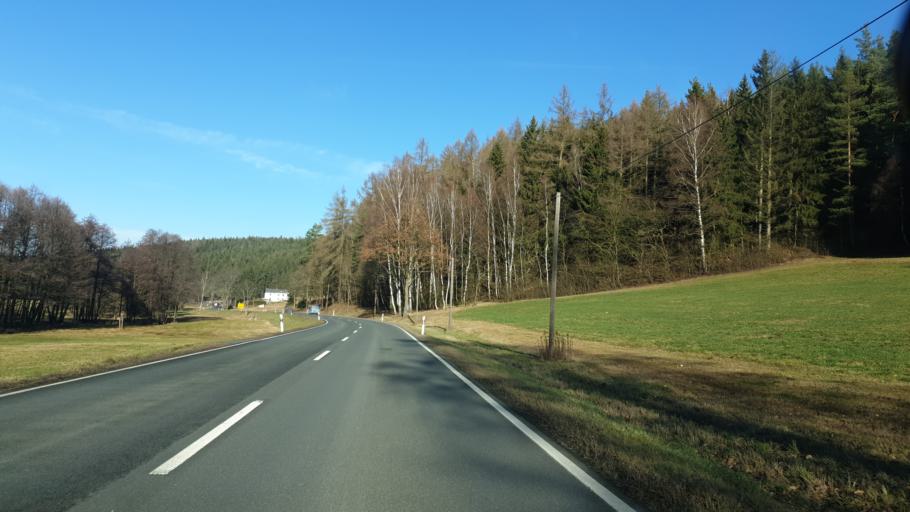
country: DE
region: Saxony
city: Bad Brambach
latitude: 50.2631
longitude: 12.3010
